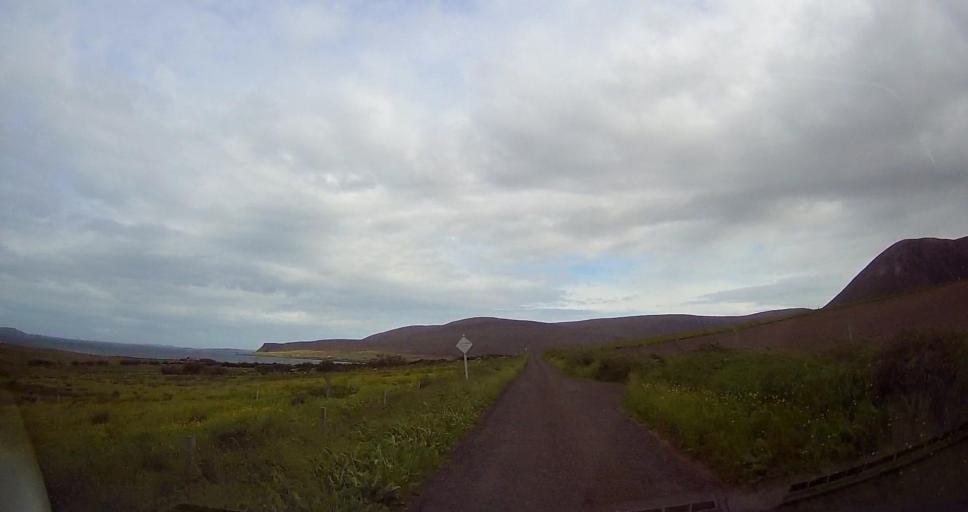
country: GB
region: Scotland
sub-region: Orkney Islands
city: Stromness
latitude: 58.9154
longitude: -3.3261
